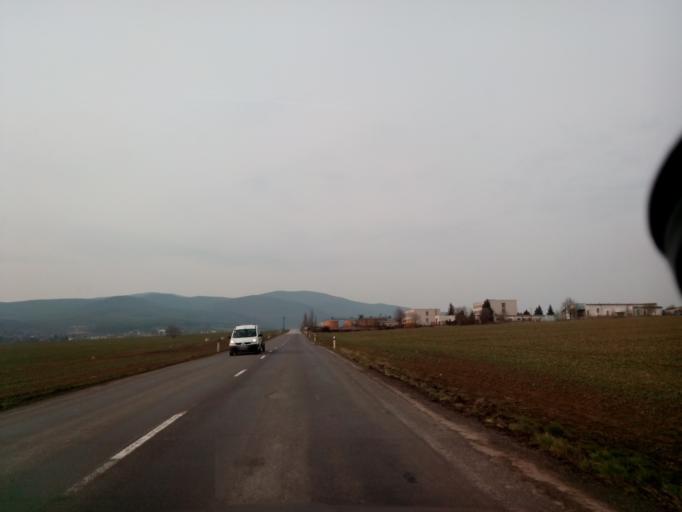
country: SK
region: Kosicky
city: Secovce
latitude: 48.6337
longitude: 21.5831
